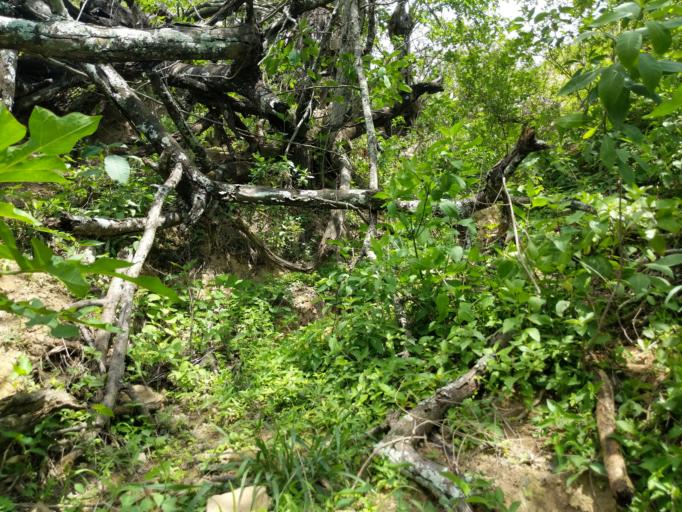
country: EC
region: Loja
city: Catacocha
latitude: -4.0051
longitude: -79.6806
